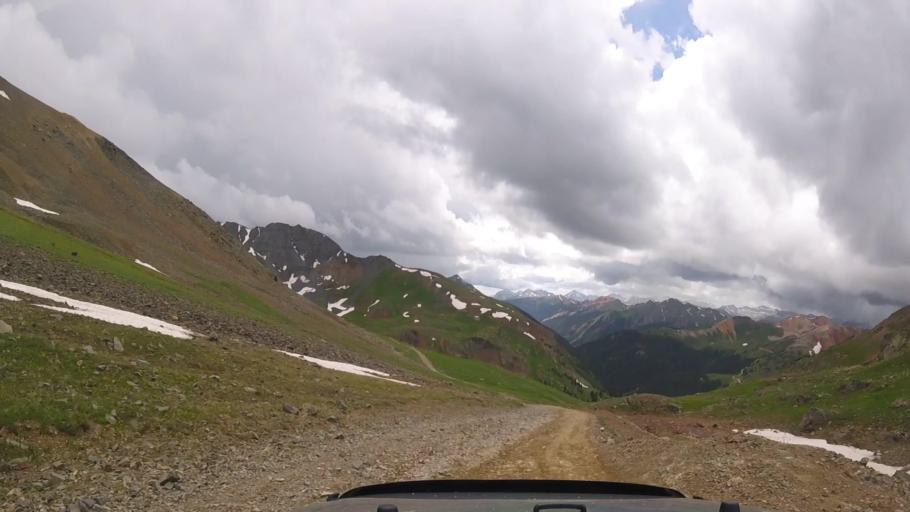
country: US
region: Colorado
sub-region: San Juan County
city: Silverton
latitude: 37.9153
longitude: -107.6276
